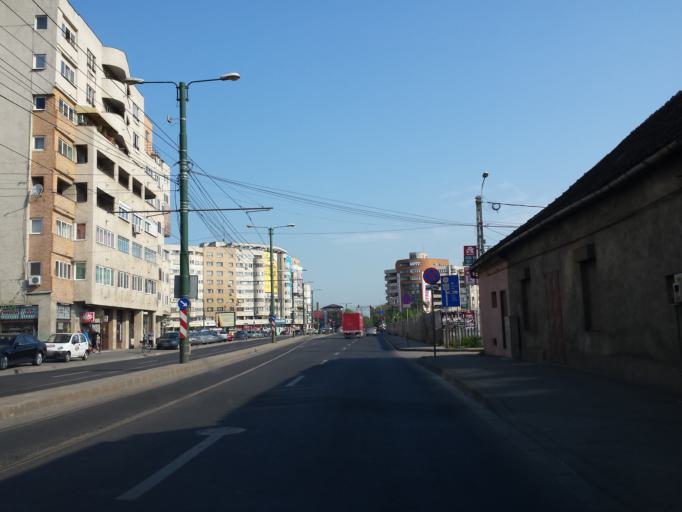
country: RO
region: Timis
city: Timisoara
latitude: 45.7639
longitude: 21.2608
